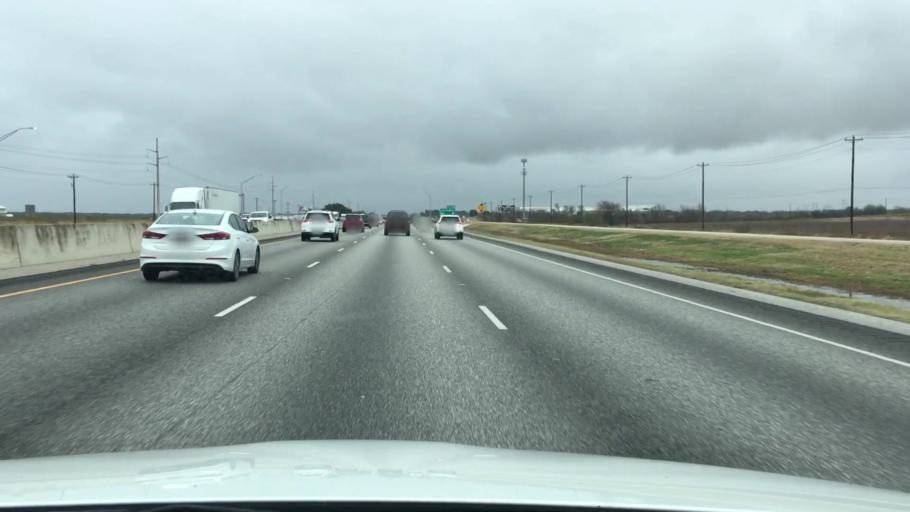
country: US
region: Texas
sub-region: Hays County
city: San Marcos
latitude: 29.9233
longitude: -97.8924
